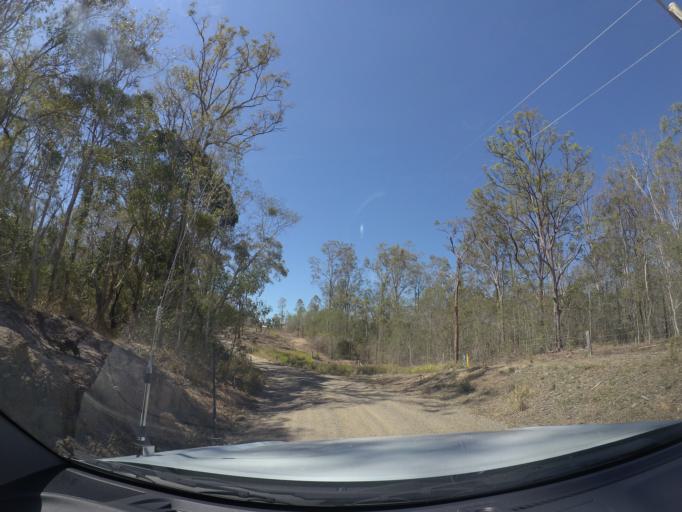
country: AU
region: Queensland
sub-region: Logan
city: North Maclean
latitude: -27.7619
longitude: 152.9415
